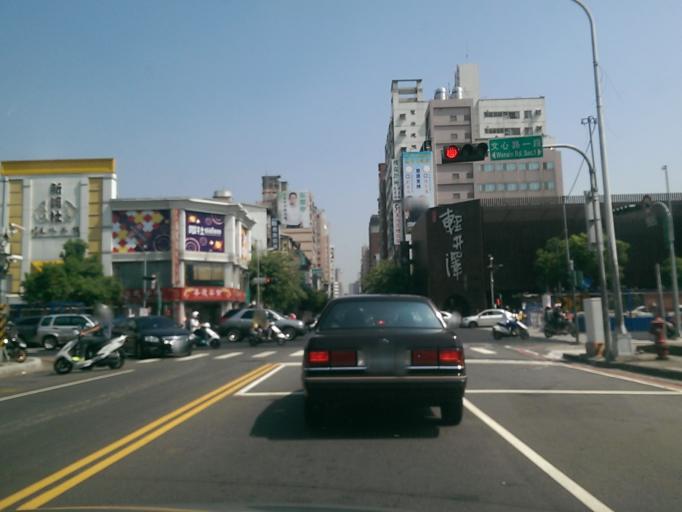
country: TW
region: Taiwan
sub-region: Taichung City
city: Taichung
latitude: 24.1537
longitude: 120.6464
